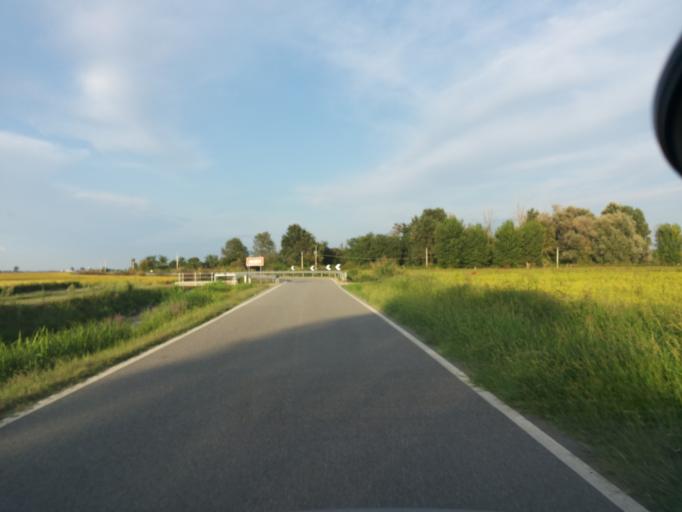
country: IT
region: Piedmont
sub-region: Provincia di Vercelli
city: Sali Vercellese
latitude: 45.3234
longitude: 8.3209
